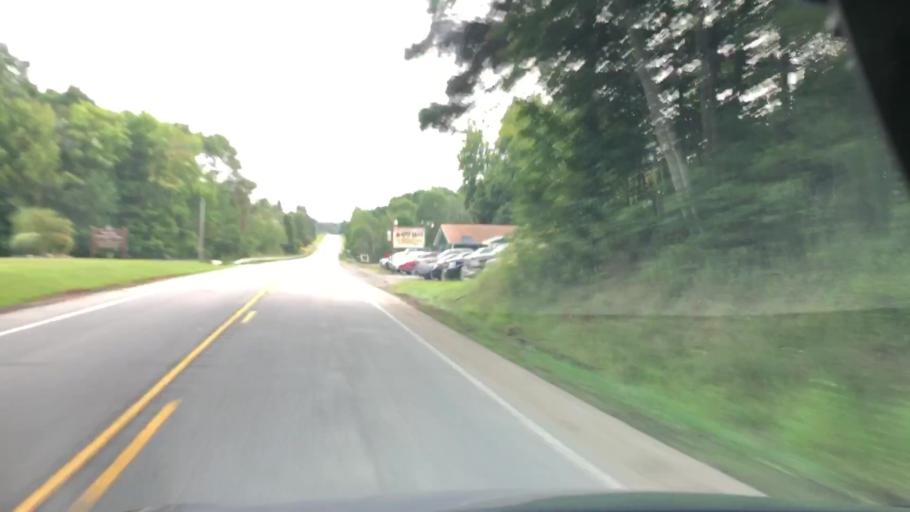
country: US
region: Pennsylvania
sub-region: Crawford County
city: Titusville
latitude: 41.6009
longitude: -79.6781
